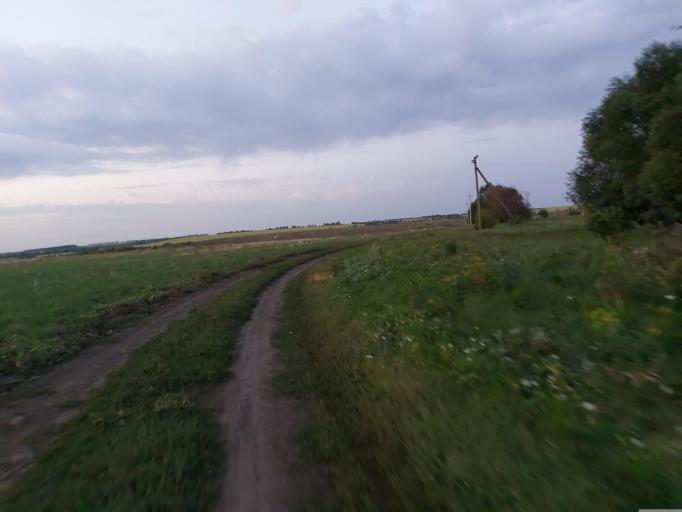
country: RU
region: Lipetsk
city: Dolgorukovo
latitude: 52.3810
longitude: 38.0439
